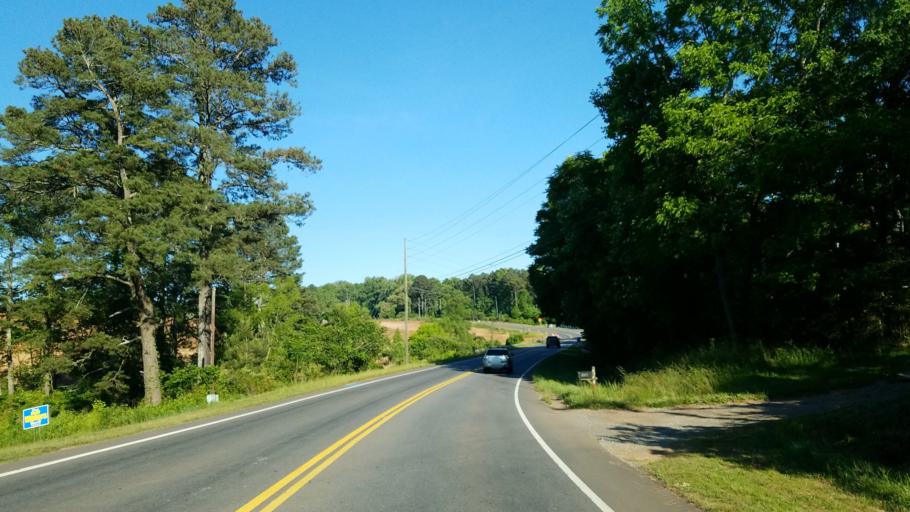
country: US
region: Georgia
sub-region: Cherokee County
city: Holly Springs
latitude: 34.1676
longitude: -84.4378
